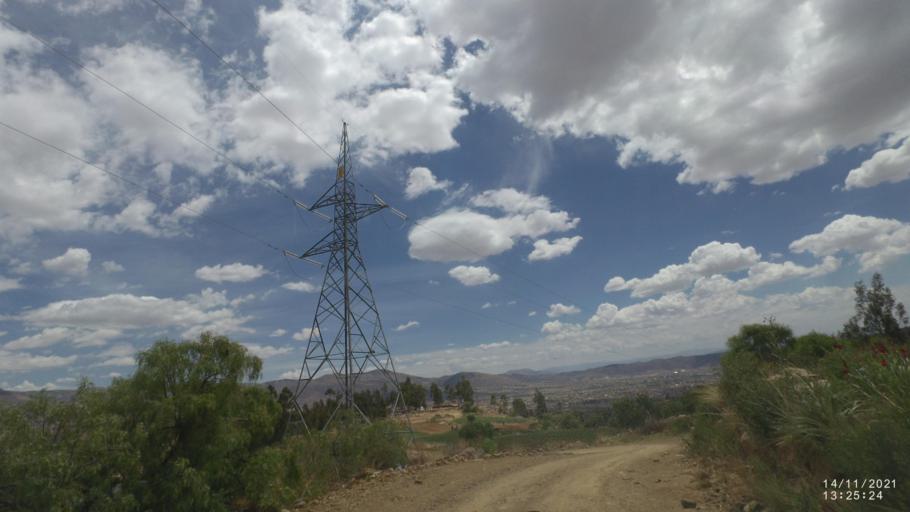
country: BO
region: Cochabamba
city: Colomi
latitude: -17.3805
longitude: -65.9804
